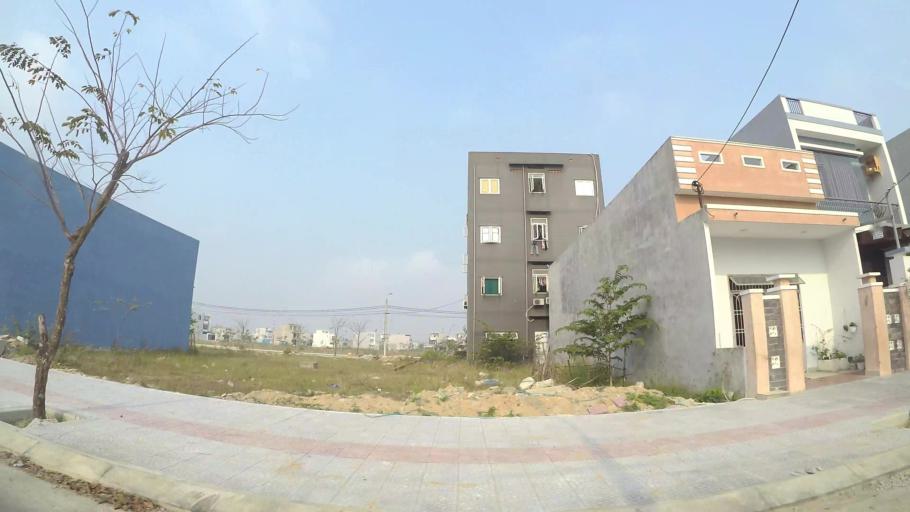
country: VN
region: Da Nang
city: Ngu Hanh Son
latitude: 16.0115
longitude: 108.2290
